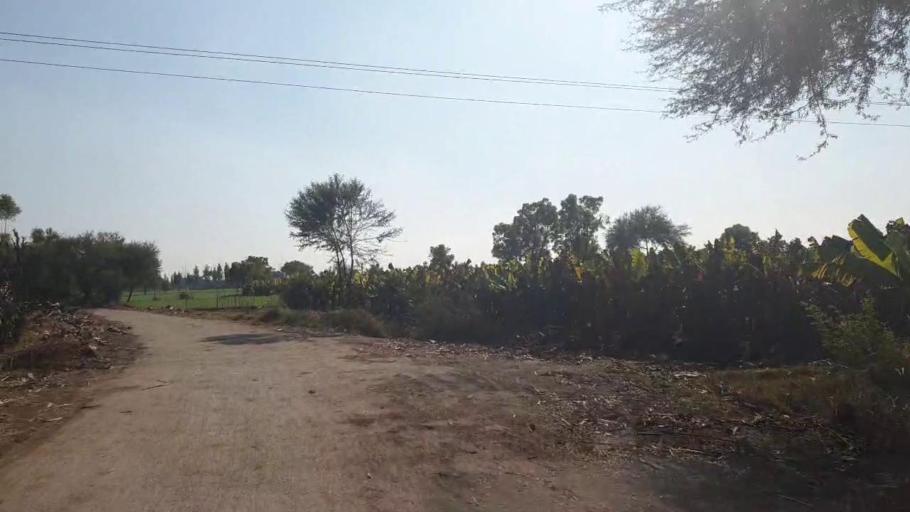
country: PK
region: Sindh
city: Shahdadpur
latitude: 25.9159
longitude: 68.5633
